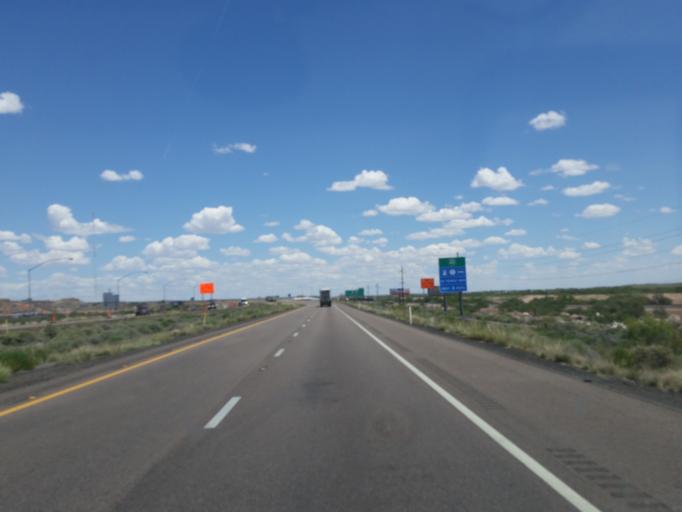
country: US
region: Arizona
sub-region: Navajo County
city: Holbrook
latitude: 34.9053
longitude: -110.1960
